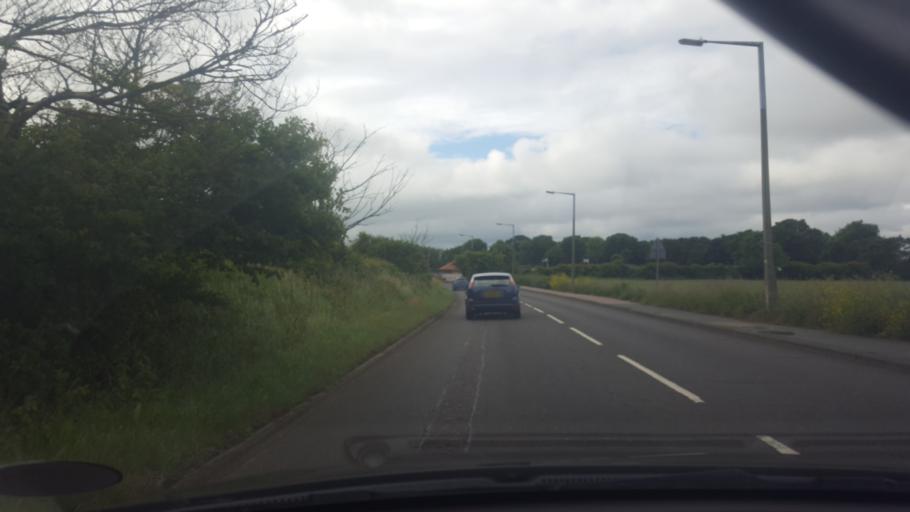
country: GB
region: England
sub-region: Essex
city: Saint Osyth
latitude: 51.7914
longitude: 1.1181
